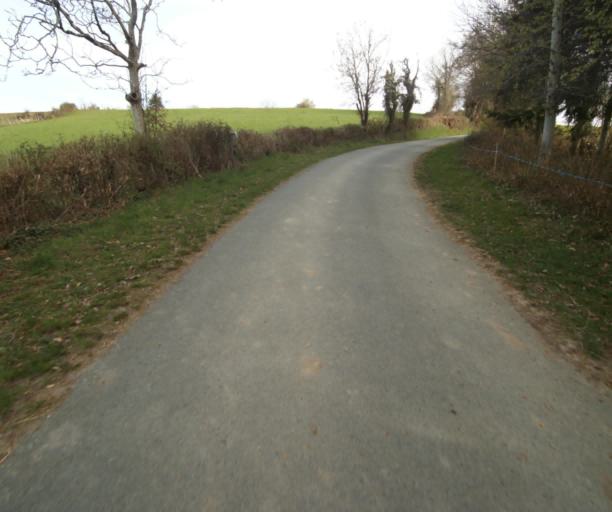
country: FR
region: Limousin
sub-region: Departement de la Correze
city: Chamboulive
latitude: 45.4338
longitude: 1.7925
